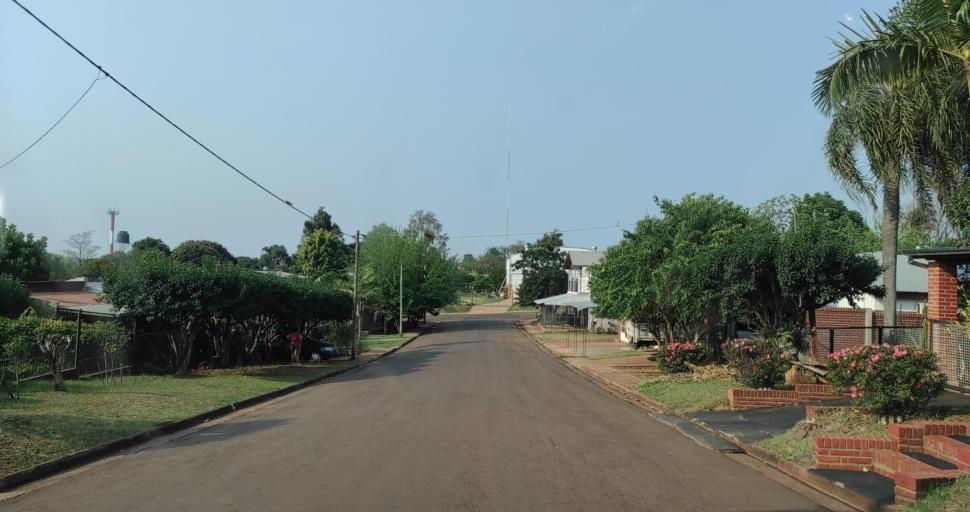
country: AR
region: Misiones
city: Cerro Azul
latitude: -27.6360
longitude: -55.4950
